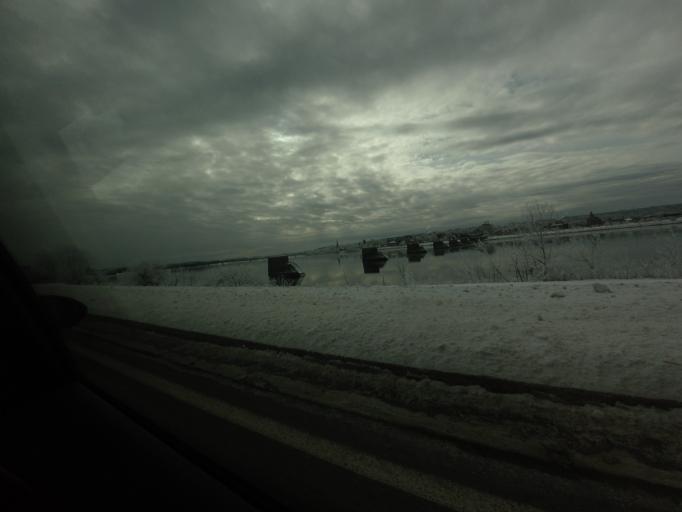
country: CA
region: New Brunswick
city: Fredericton
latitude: 45.9696
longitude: -66.6357
